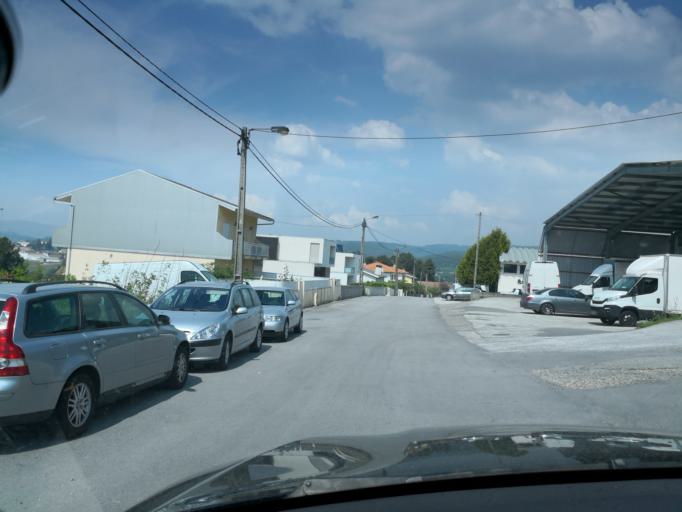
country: PT
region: Vila Real
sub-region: Vila Real
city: Vila Real
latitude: 41.2830
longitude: -7.7212
